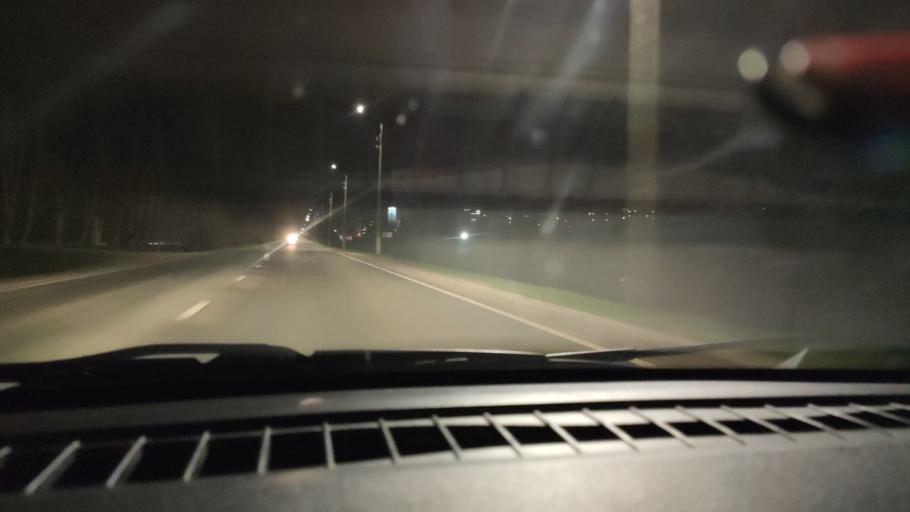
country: RU
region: Bashkortostan
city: Sterlitamak
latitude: 53.6459
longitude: 55.8863
